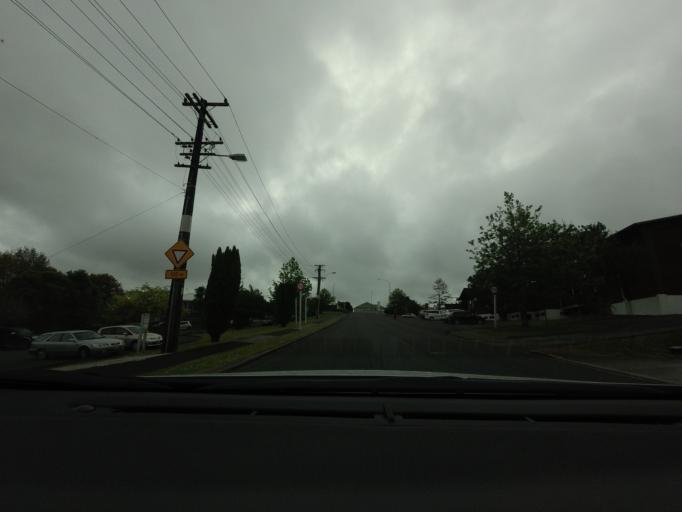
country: NZ
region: Auckland
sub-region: Auckland
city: Wellsford
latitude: -36.2922
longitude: 174.5254
